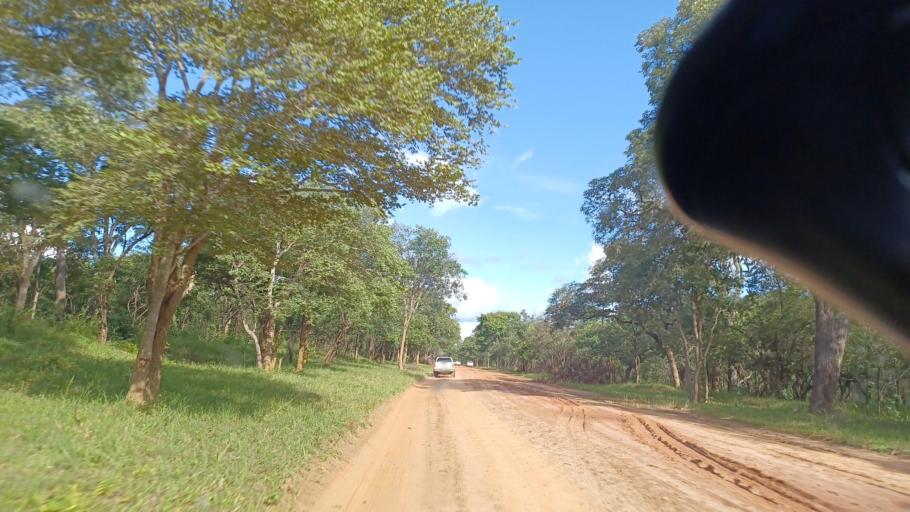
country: ZM
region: North-Western
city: Kabompo
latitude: -13.3509
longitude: 24.2842
